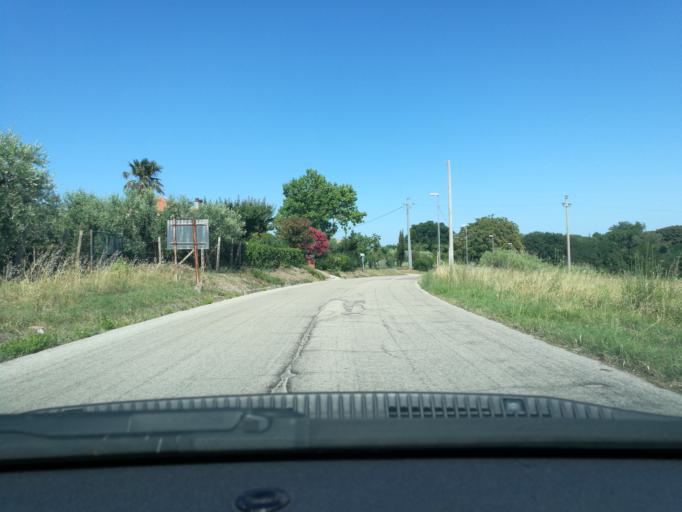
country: IT
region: Abruzzo
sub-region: Provincia di Chieti
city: Vasto
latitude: 42.1665
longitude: 14.6936
